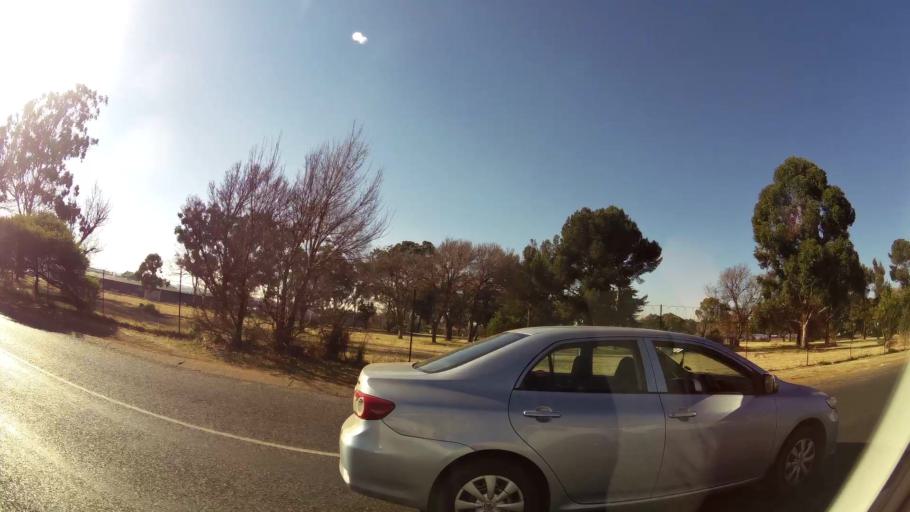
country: ZA
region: Gauteng
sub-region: Ekurhuleni Metropolitan Municipality
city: Germiston
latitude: -26.2821
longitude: 28.1218
